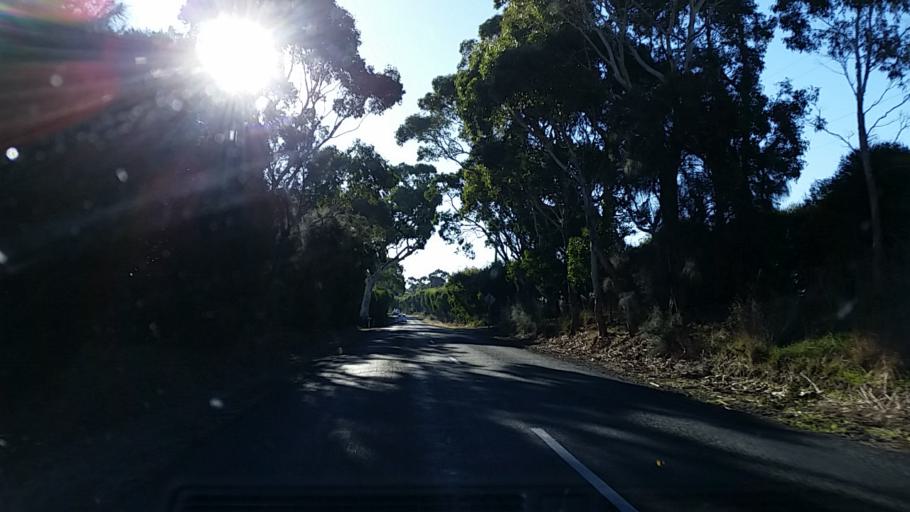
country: AU
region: South Australia
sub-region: Mount Barker
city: Mount Barker
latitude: -35.1222
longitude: 138.8997
